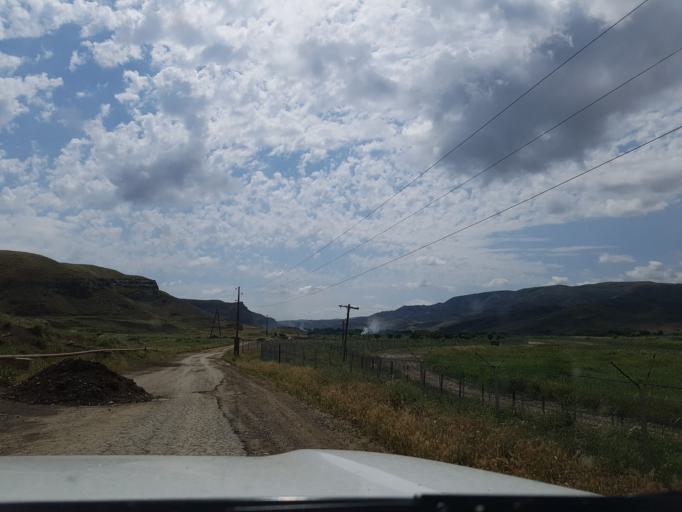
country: TM
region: Ahal
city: Baharly
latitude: 38.2297
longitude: 56.8666
